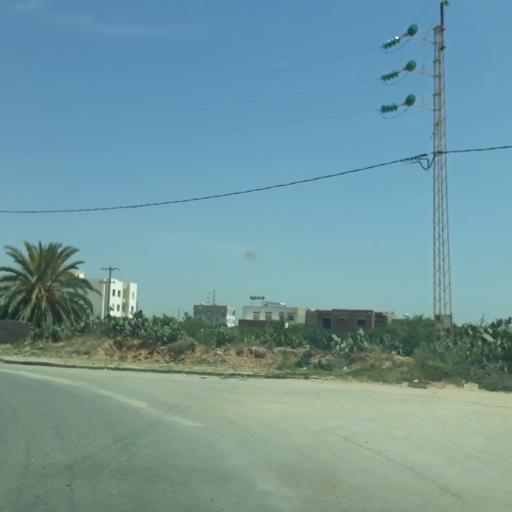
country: TN
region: Safaqis
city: Al Qarmadah
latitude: 34.8144
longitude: 10.7721
